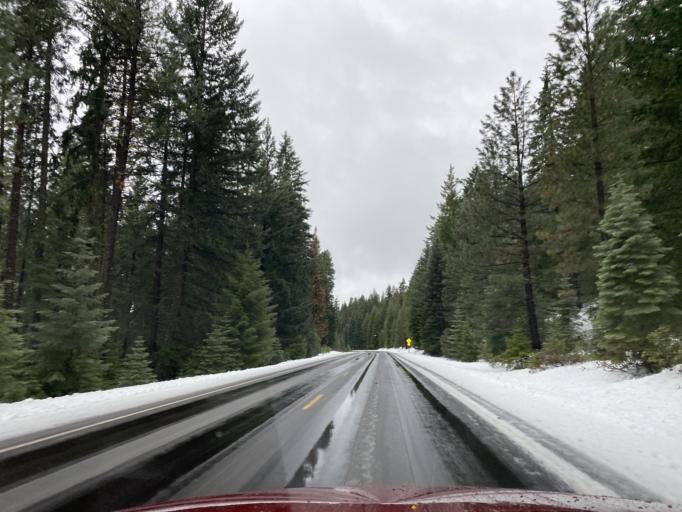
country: US
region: Oregon
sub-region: Klamath County
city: Klamath Falls
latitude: 42.4982
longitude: -122.0844
